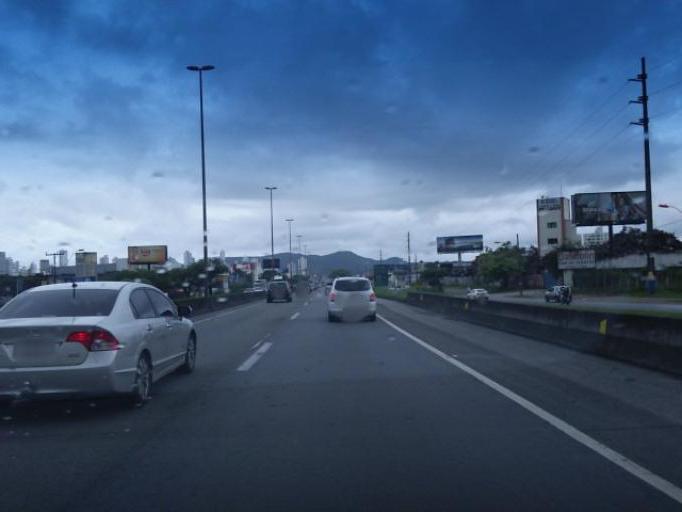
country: BR
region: Santa Catarina
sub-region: Balneario Camboriu
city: Balneario Camboriu
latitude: -26.9974
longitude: -48.6526
